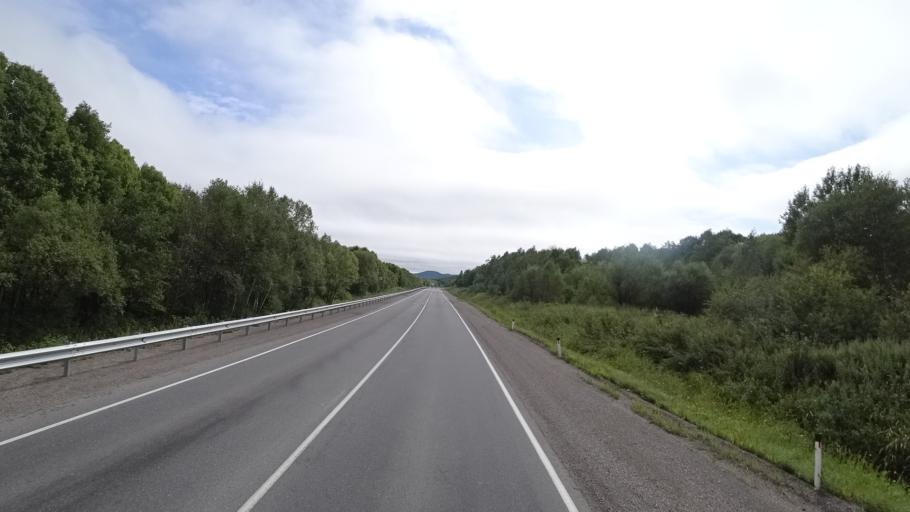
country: RU
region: Primorskiy
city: Lyalichi
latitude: 44.1166
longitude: 132.4191
